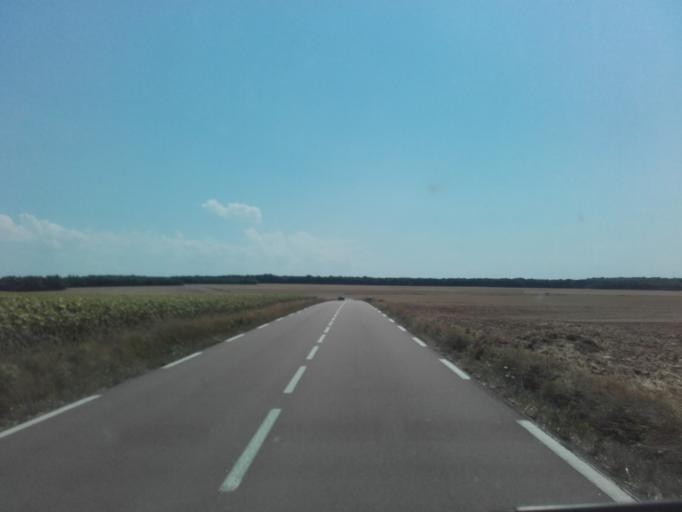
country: FR
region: Bourgogne
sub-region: Departement de l'Yonne
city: Joux-la-Ville
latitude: 47.7167
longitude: 3.8528
